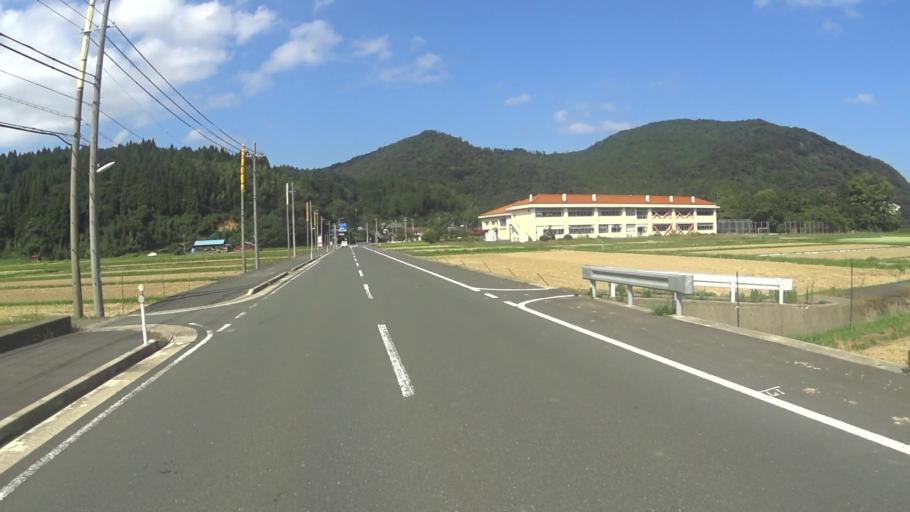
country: JP
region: Kyoto
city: Miyazu
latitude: 35.7271
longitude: 135.2553
